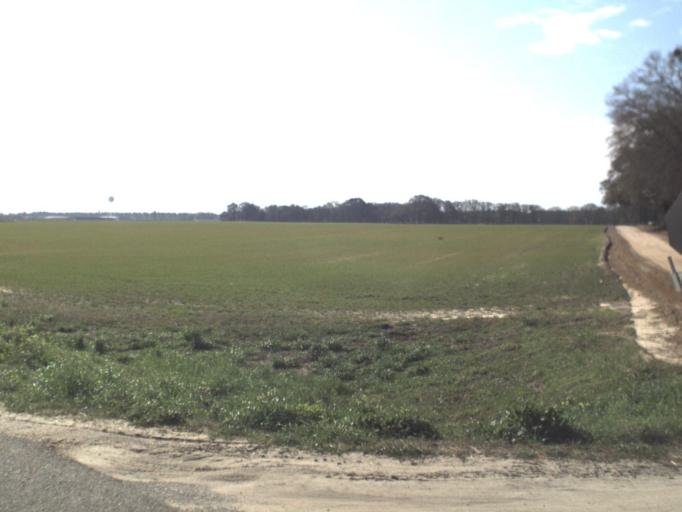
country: US
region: Florida
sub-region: Jackson County
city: Malone
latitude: 30.9798
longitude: -85.1764
